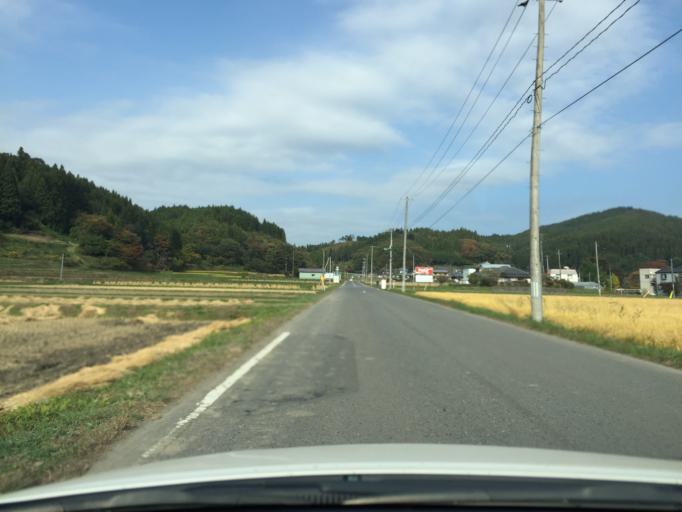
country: JP
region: Fukushima
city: Ishikawa
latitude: 36.9844
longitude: 140.4830
